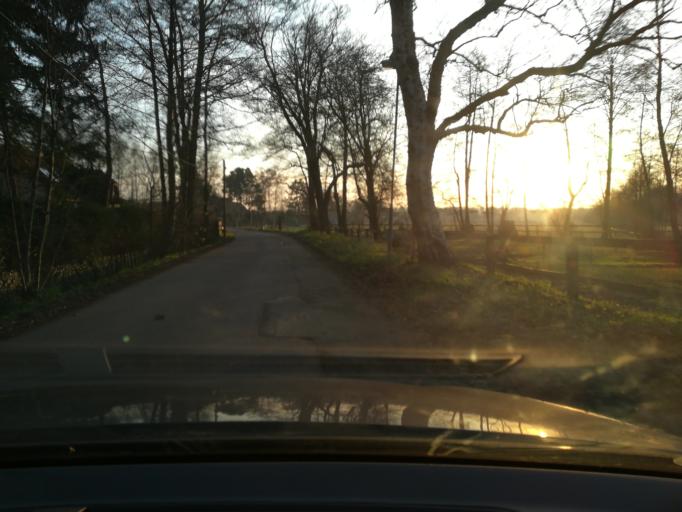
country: DE
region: Schleswig-Holstein
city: Escheburg
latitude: 53.4494
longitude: 10.3003
